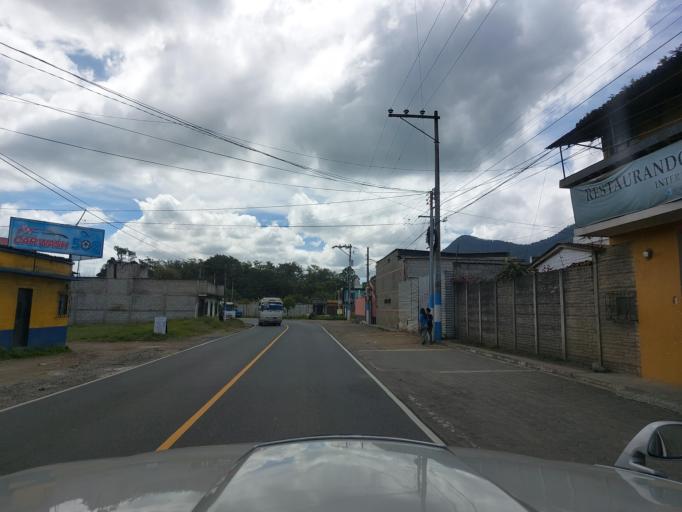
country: GT
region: Chimaltenango
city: Parramos
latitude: 14.6096
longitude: -90.7990
